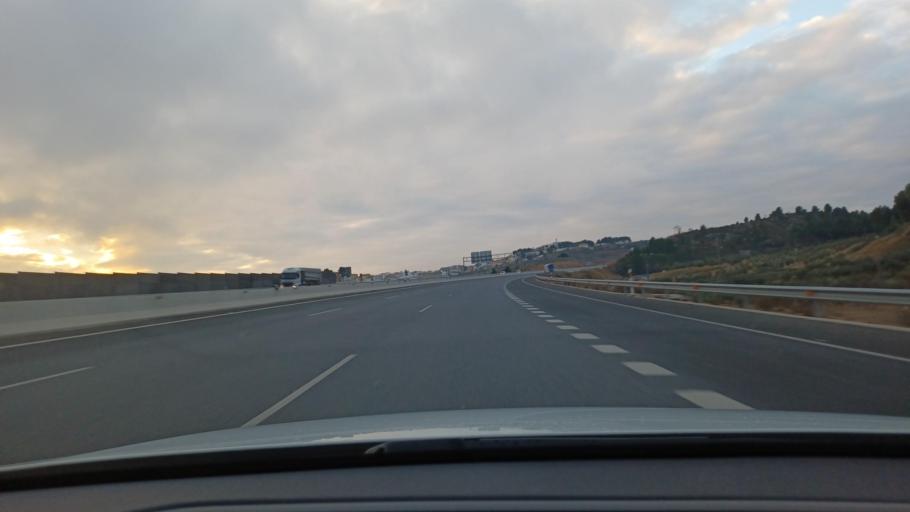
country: ES
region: Valencia
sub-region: Provincia de Valencia
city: La Font de la Figuera
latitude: 38.8134
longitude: -0.8869
